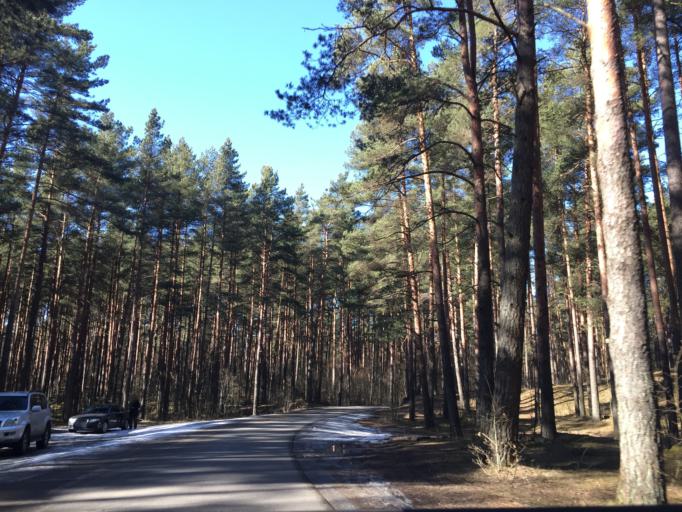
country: LV
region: Marupe
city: Marupe
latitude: 56.9643
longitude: 23.9956
